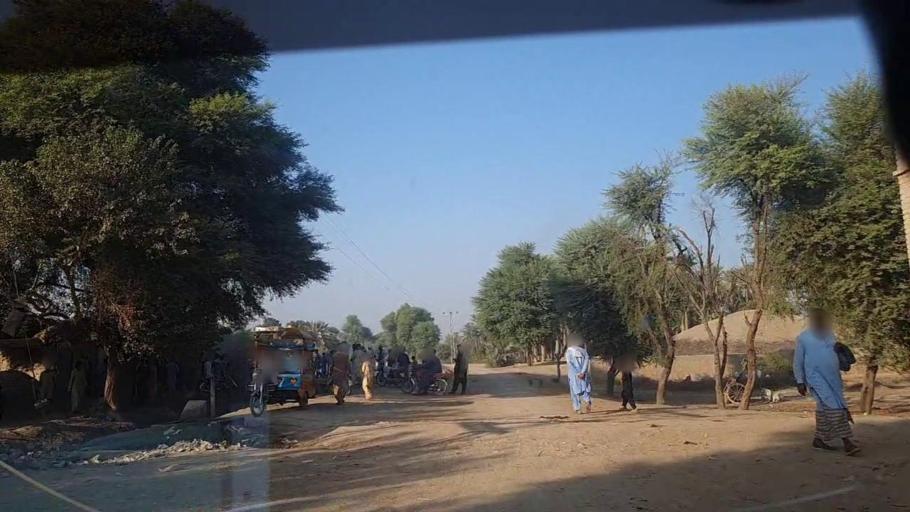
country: PK
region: Sindh
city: Sobhadero
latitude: 27.2576
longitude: 68.3510
